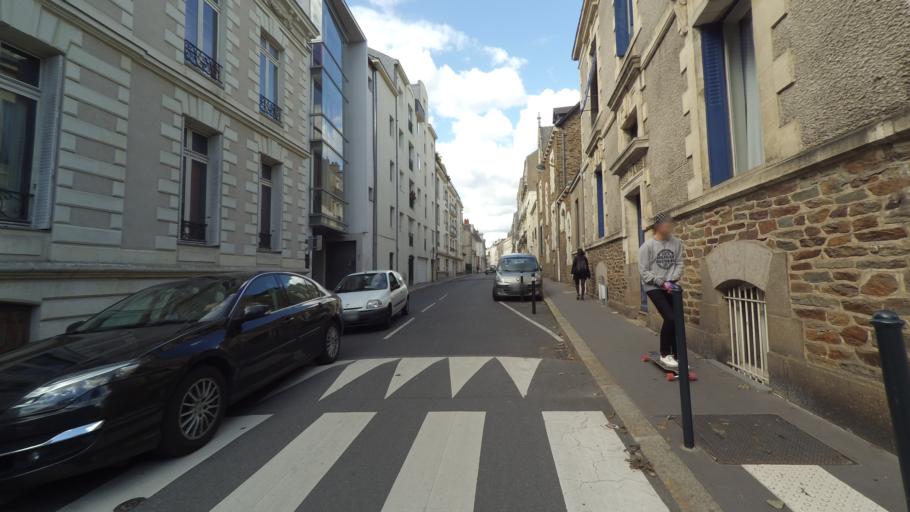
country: FR
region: Pays de la Loire
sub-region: Departement de la Loire-Atlantique
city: Nantes
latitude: 47.2131
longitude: -1.5672
